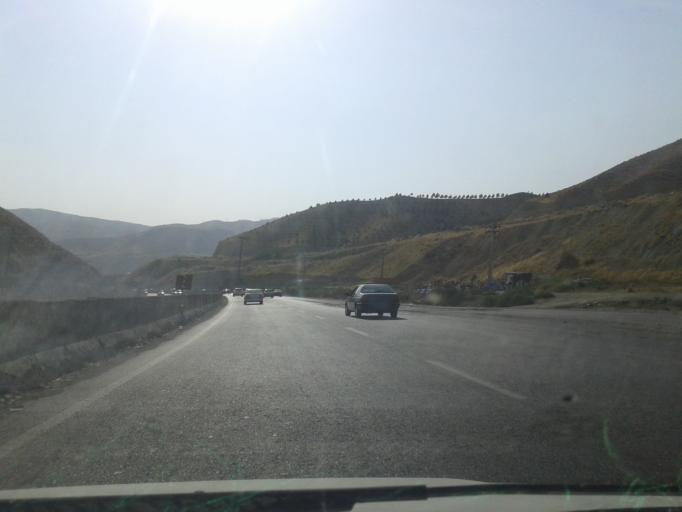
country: IR
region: Tehran
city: Pakdasht
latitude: 35.7480
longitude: 51.7127
